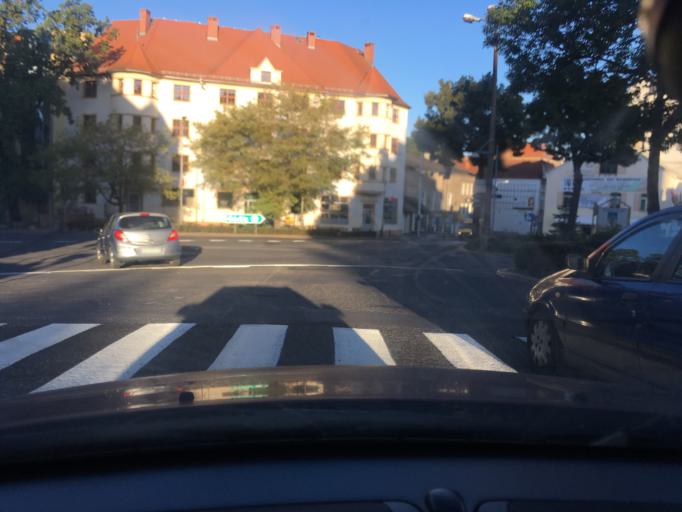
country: PL
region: Lower Silesian Voivodeship
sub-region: Powiat zgorzelecki
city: Zgorzelec
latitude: 51.1497
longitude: 15.0070
